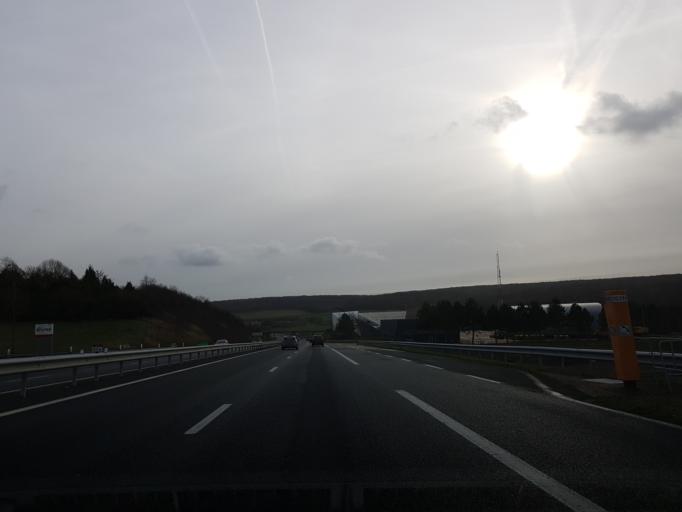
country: FR
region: Bourgogne
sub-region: Departement de l'Yonne
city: Soucy
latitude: 48.2534
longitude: 3.3372
